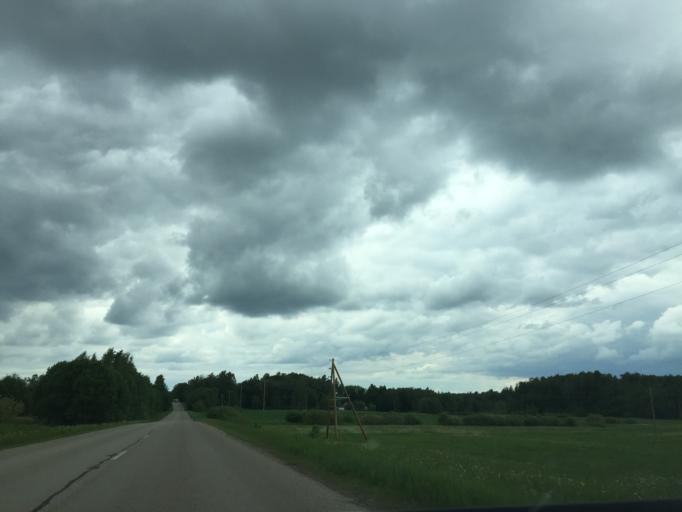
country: LV
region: Dagda
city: Dagda
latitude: 56.1131
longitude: 27.4822
